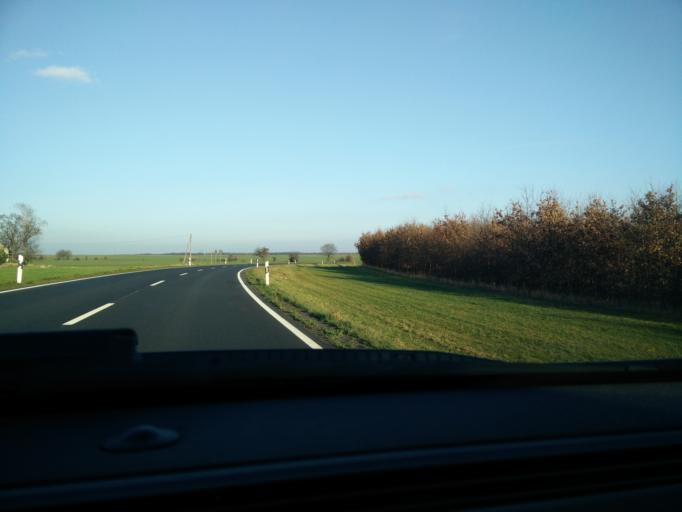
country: DE
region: Saxony
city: Bad Lausick
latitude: 51.1583
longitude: 12.6468
